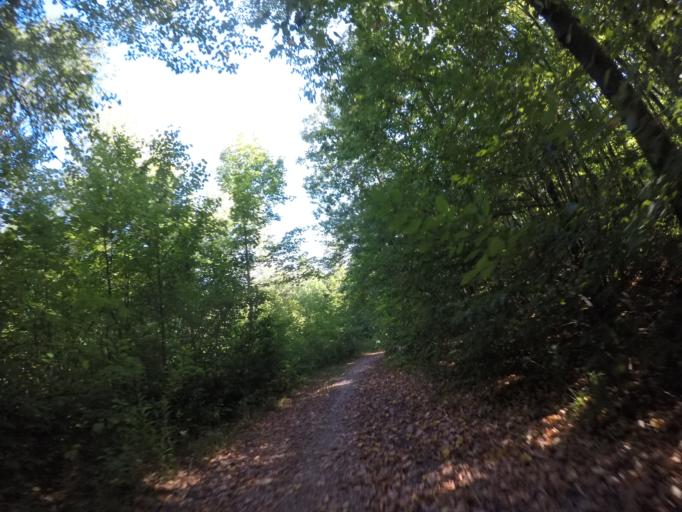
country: SK
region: Kosicky
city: Kosice
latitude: 48.7424
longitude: 21.2089
